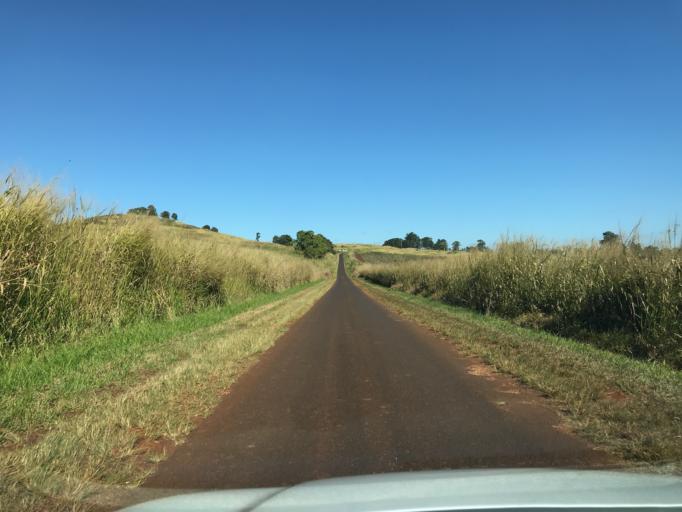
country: AU
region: Queensland
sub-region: Tablelands
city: Atherton
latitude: -17.2874
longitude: 145.5430
